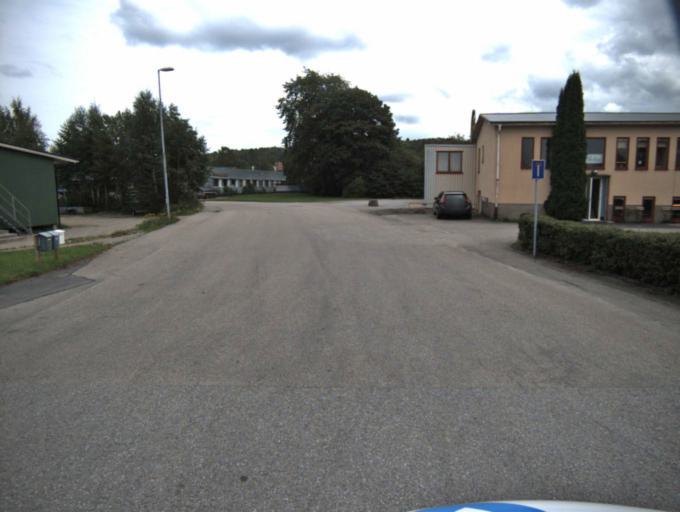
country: SE
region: Vaestra Goetaland
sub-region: Ulricehamns Kommun
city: Ulricehamn
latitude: 57.8007
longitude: 13.4128
